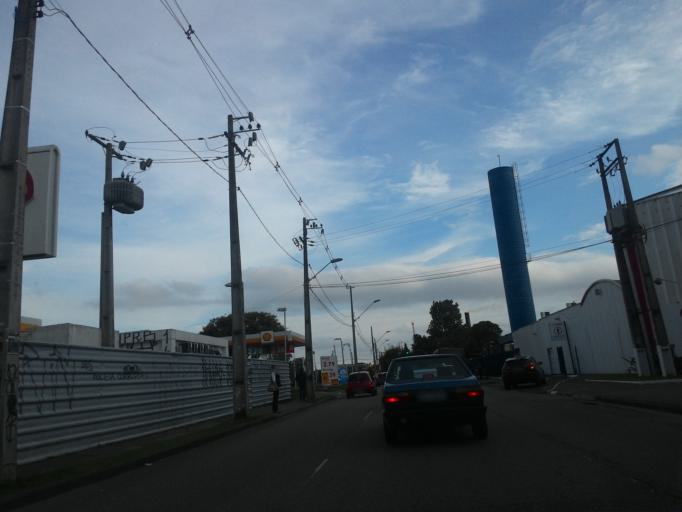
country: BR
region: Parana
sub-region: Curitiba
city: Curitiba
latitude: -25.4360
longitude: -49.2611
